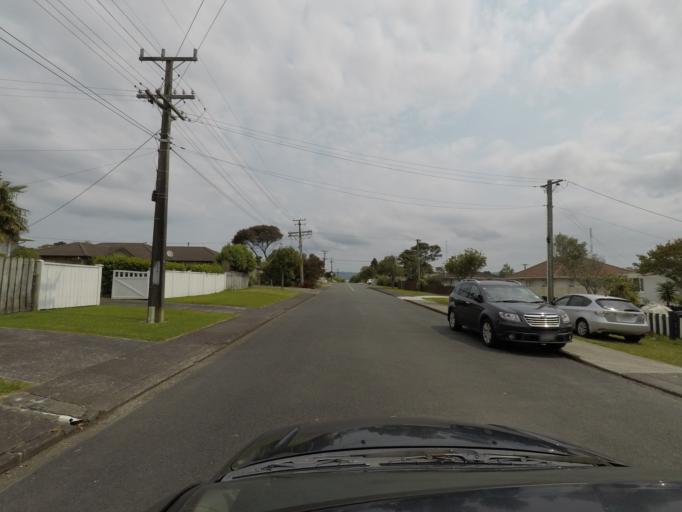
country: NZ
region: Auckland
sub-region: Auckland
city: Rosebank
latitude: -36.8410
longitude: 174.6395
